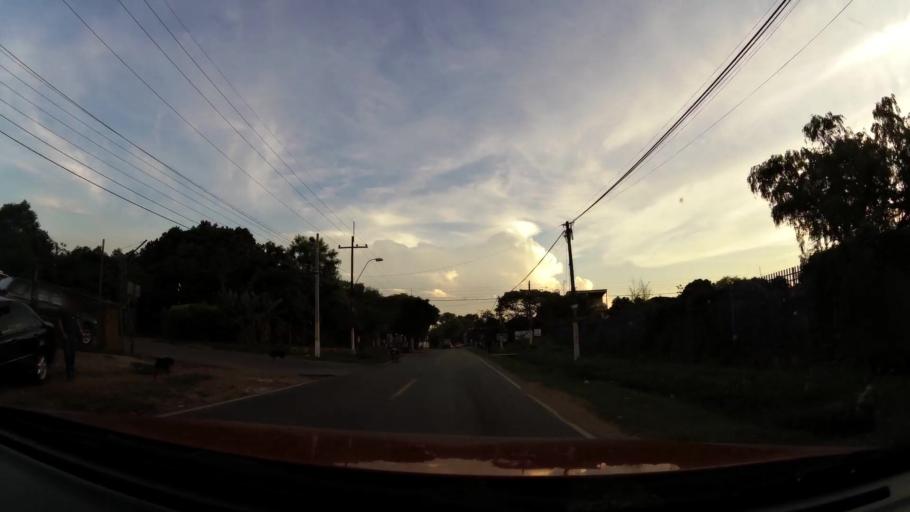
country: PY
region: Central
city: San Lorenzo
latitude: -25.3557
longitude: -57.4909
